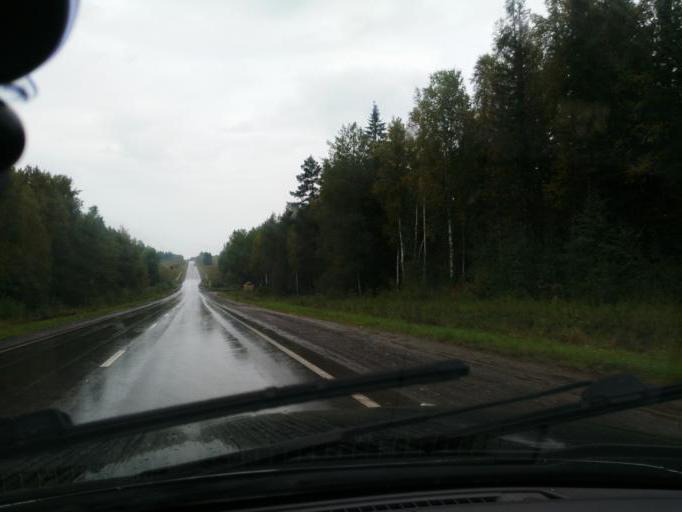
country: RU
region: Perm
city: Yugo-Kamskiy
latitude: 57.4830
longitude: 55.6813
